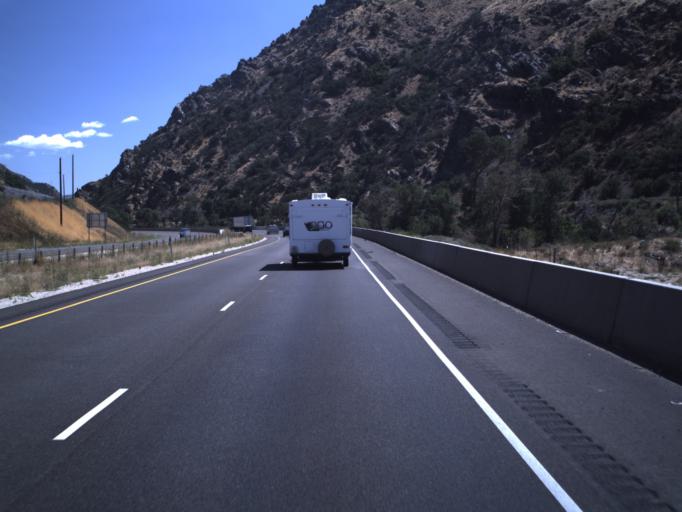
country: US
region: Utah
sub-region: Weber County
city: Uintah
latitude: 41.1363
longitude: -111.9002
